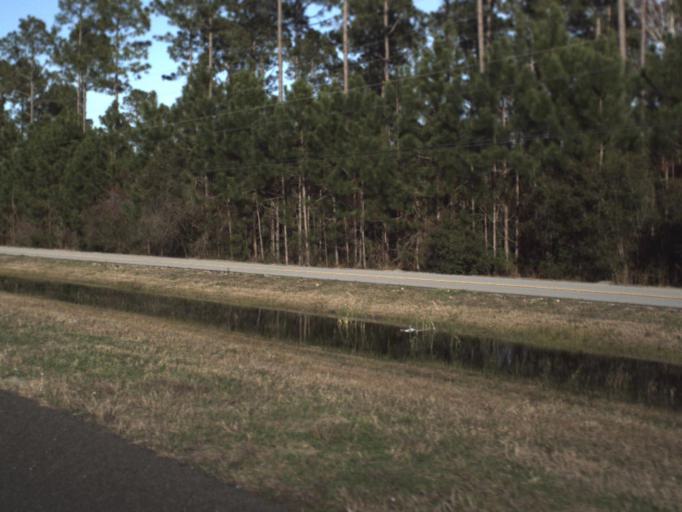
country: US
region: Florida
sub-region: Bay County
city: Laguna Beach
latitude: 30.2847
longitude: -85.8641
